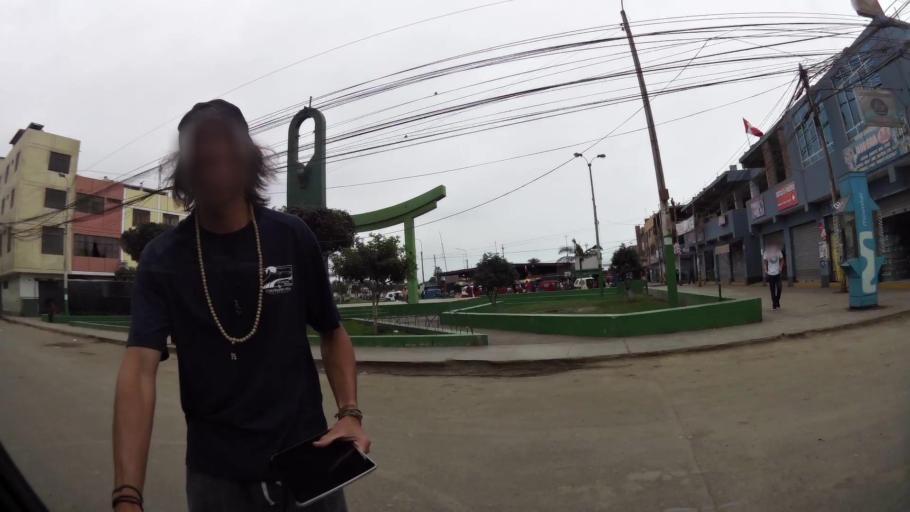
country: PE
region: Lima
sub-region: Barranca
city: Paramonga
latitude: -10.6736
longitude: -77.8193
